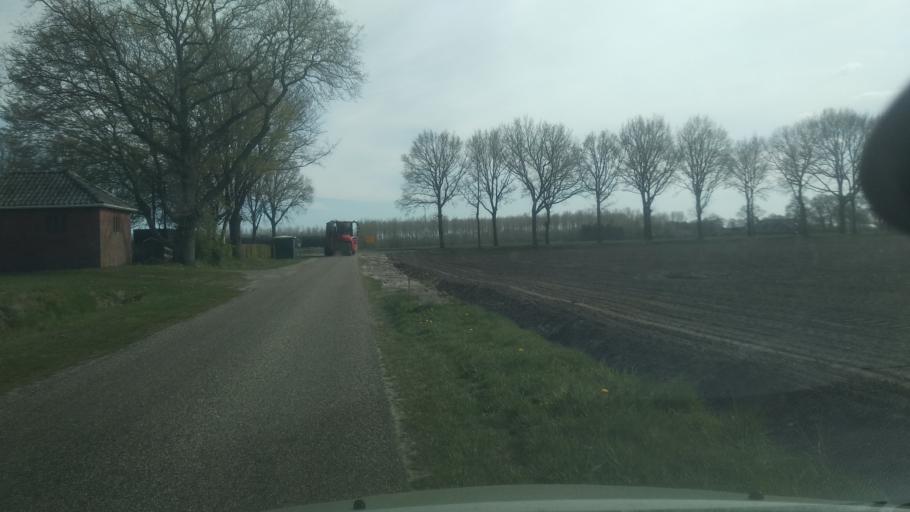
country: NL
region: Drenthe
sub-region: Gemeente Borger-Odoorn
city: Borger
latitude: 52.9680
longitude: 6.8636
